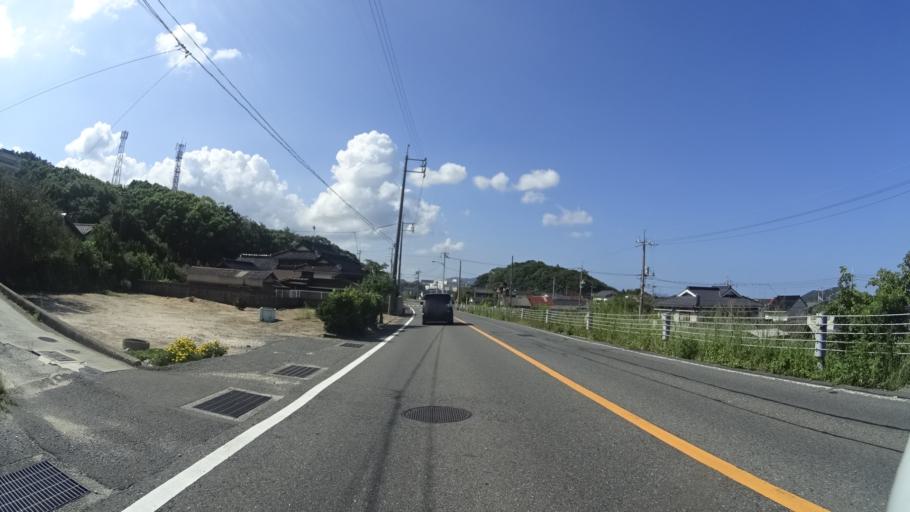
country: JP
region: Yamaguchi
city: Shimonoseki
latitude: 34.1742
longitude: 130.9307
